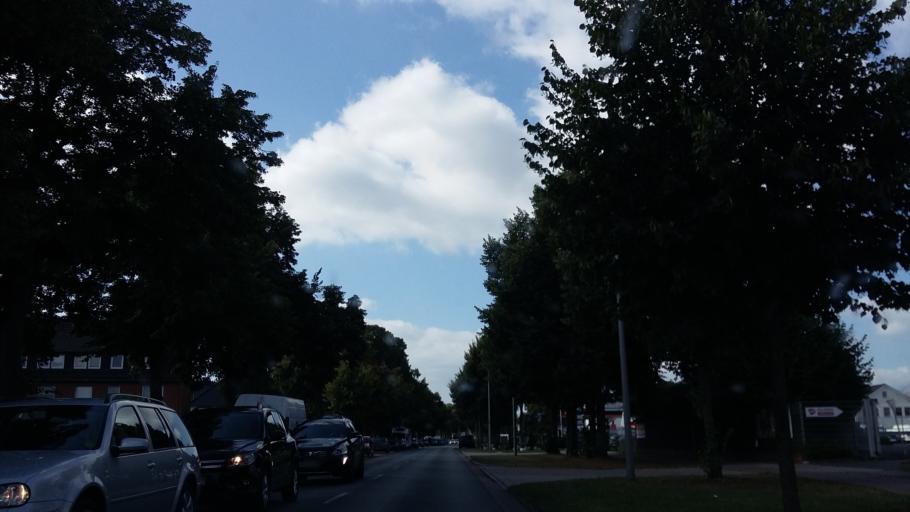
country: DE
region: Bremen
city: Bremen
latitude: 53.0401
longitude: 8.8330
